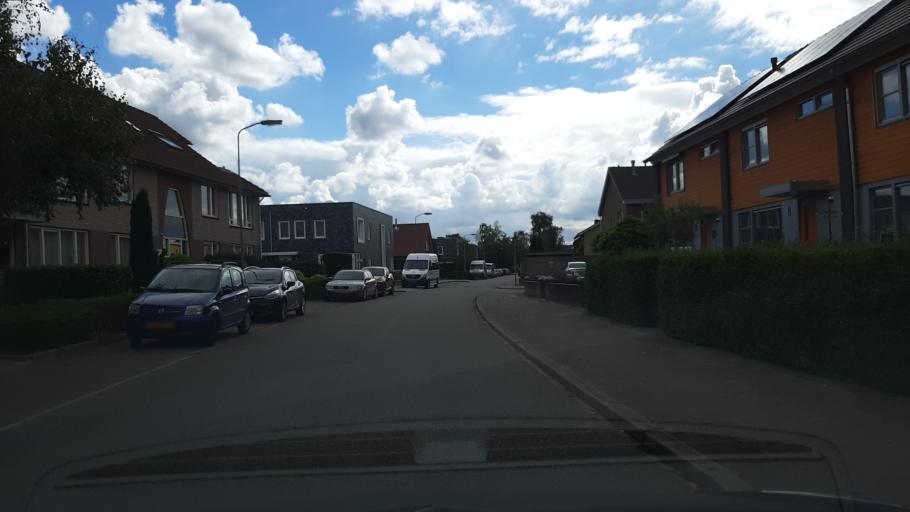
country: NL
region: Gelderland
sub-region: Gemeente Ermelo
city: Ermelo
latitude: 52.2972
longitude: 5.6278
